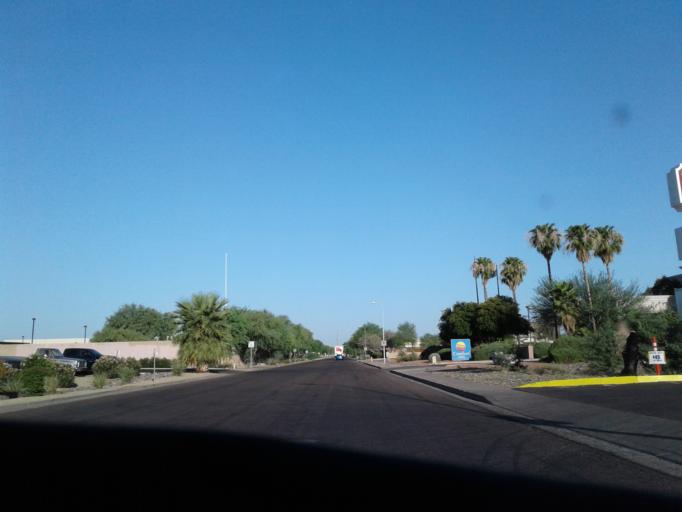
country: US
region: Arizona
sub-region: Maricopa County
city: Glendale
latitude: 33.4605
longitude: -112.1707
